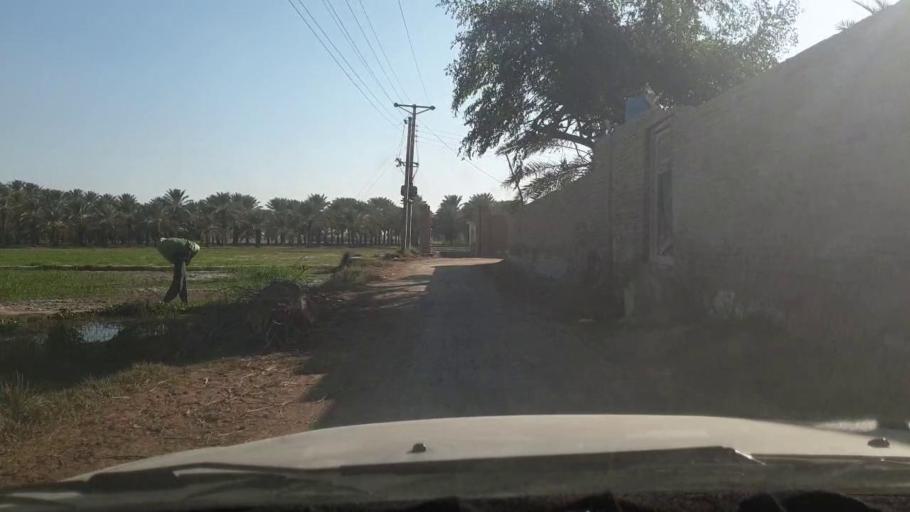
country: PK
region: Sindh
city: Ghotki
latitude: 28.0567
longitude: 69.3241
